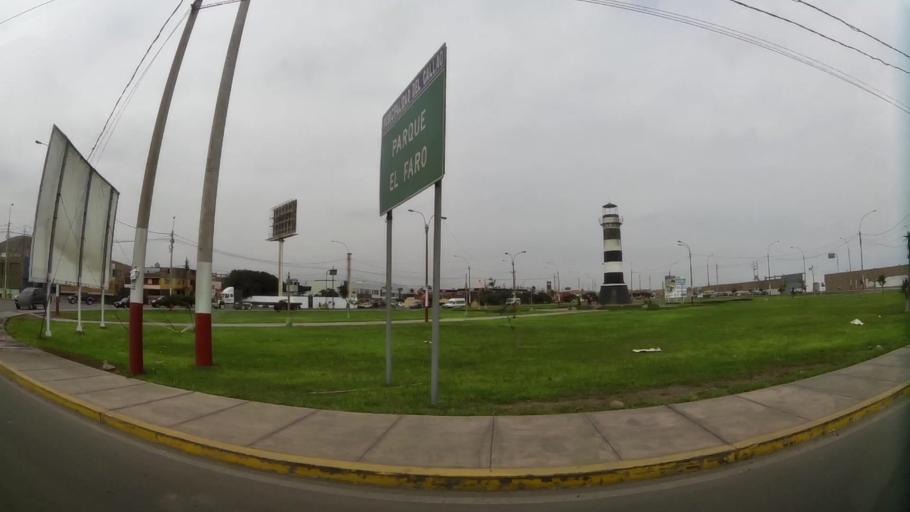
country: PE
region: Callao
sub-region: Callao
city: Callao
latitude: -11.9968
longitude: -77.1262
